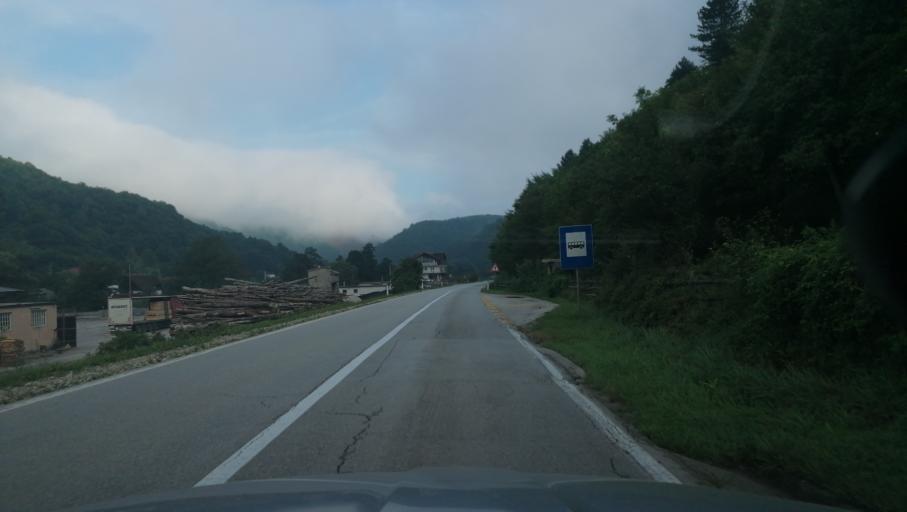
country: BA
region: Federation of Bosnia and Herzegovina
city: Donji Vakuf
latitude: 44.1762
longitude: 17.3564
